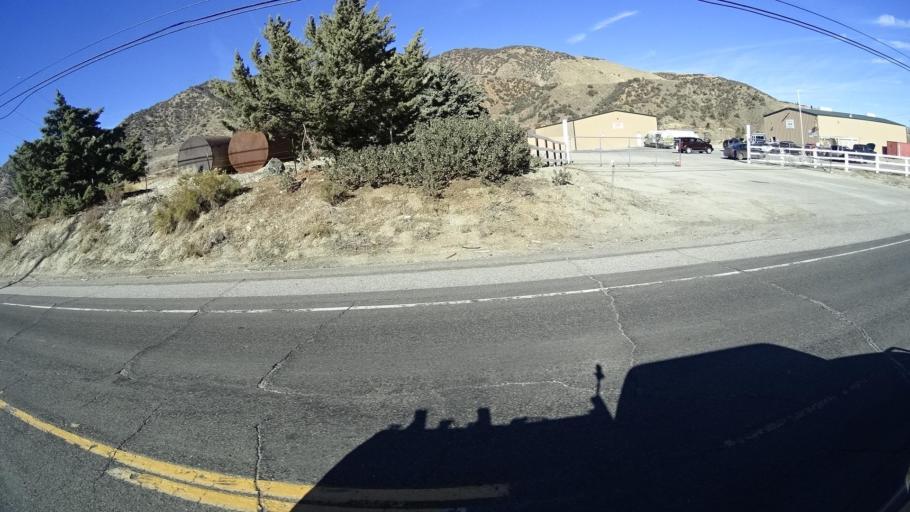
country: US
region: California
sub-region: Kern County
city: Frazier Park
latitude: 34.8171
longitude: -118.9067
